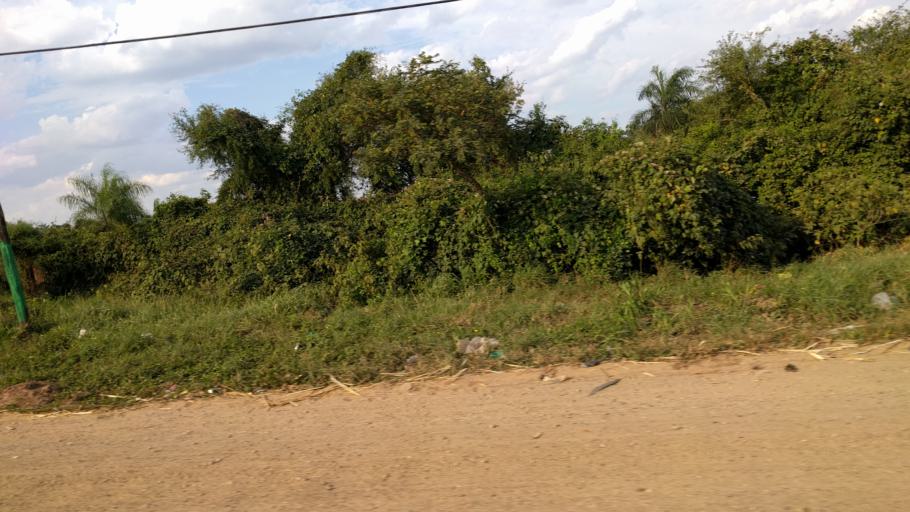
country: BO
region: Santa Cruz
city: Warnes
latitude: -17.5246
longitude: -63.1619
